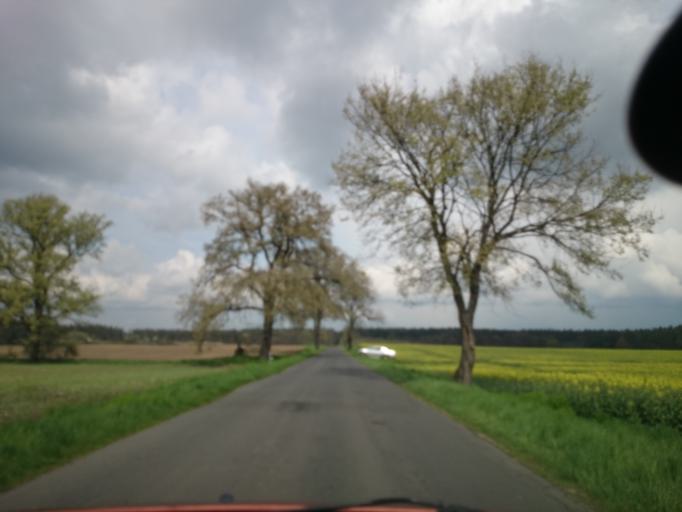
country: PL
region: Opole Voivodeship
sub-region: Powiat strzelecki
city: Izbicko
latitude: 50.5311
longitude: 18.1312
